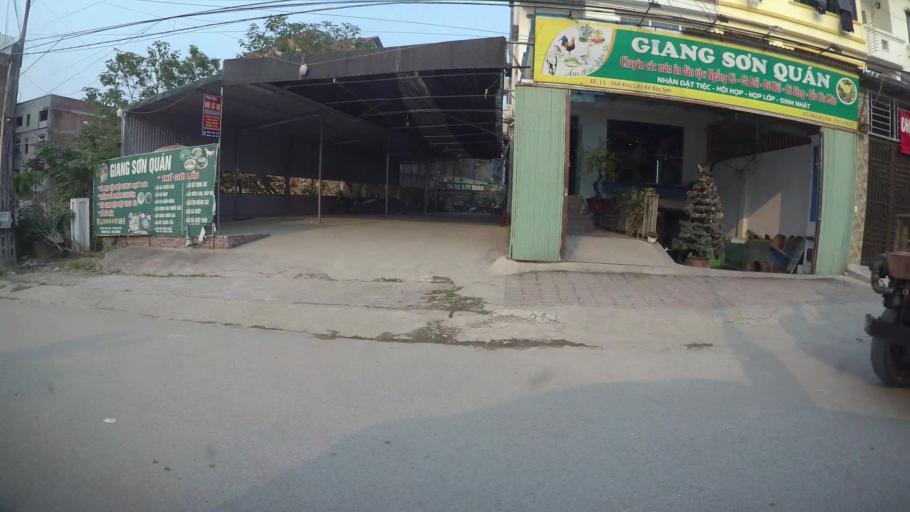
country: VN
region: Ha Noi
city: Cau Dien
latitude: 21.0024
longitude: 105.7332
